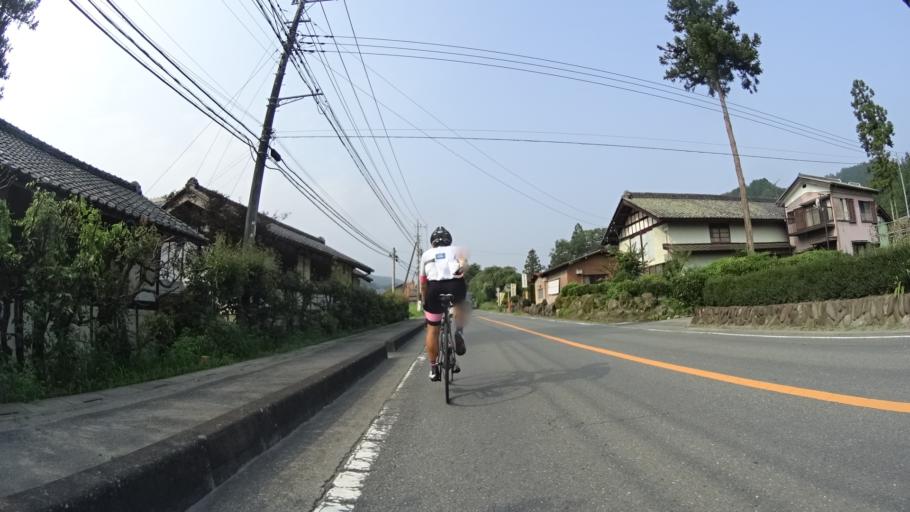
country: JP
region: Saitama
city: Chichibu
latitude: 36.0287
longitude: 139.0725
